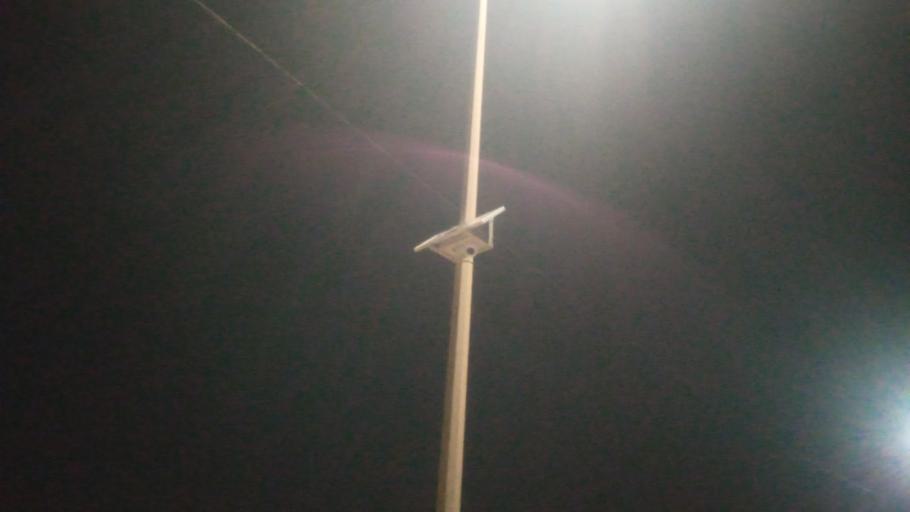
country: TN
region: Madanin
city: Midoun
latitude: 33.7390
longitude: 10.9184
